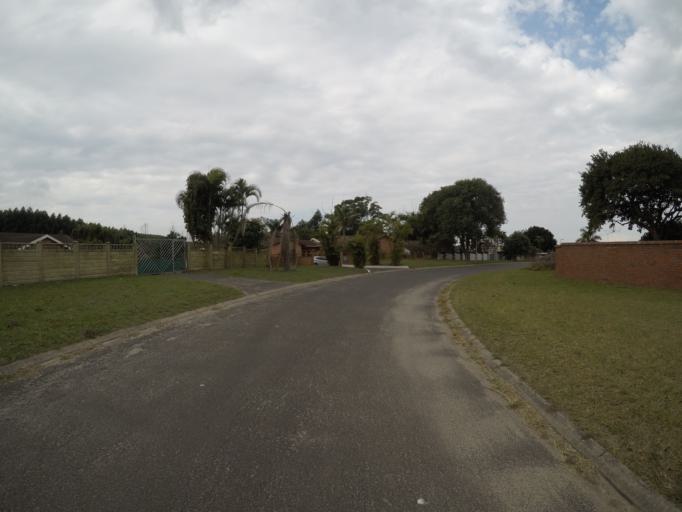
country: ZA
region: KwaZulu-Natal
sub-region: uThungulu District Municipality
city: Richards Bay
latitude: -28.7313
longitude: 32.0568
